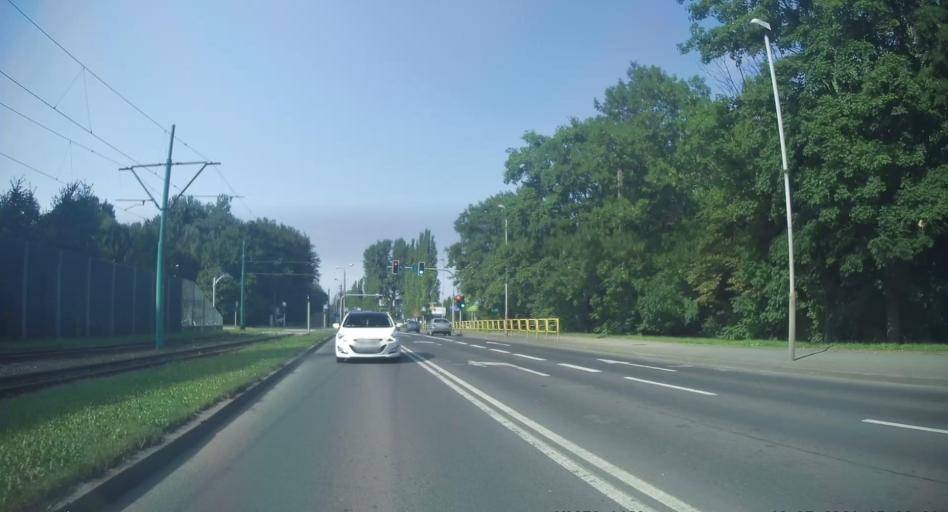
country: PL
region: Silesian Voivodeship
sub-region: Swietochlowice
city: Swietochlowice
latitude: 50.2978
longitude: 18.9177
